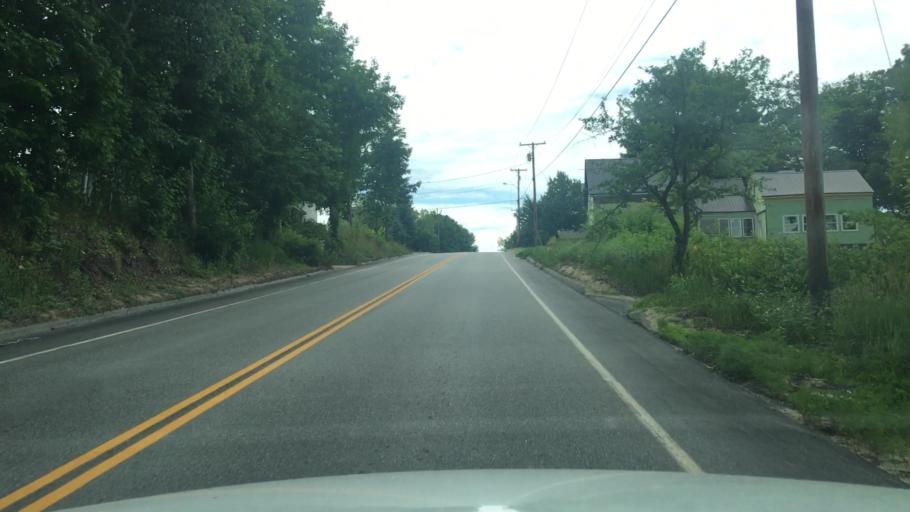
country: US
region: Maine
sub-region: Oxford County
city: Hartford
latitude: 44.3655
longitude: -70.4587
